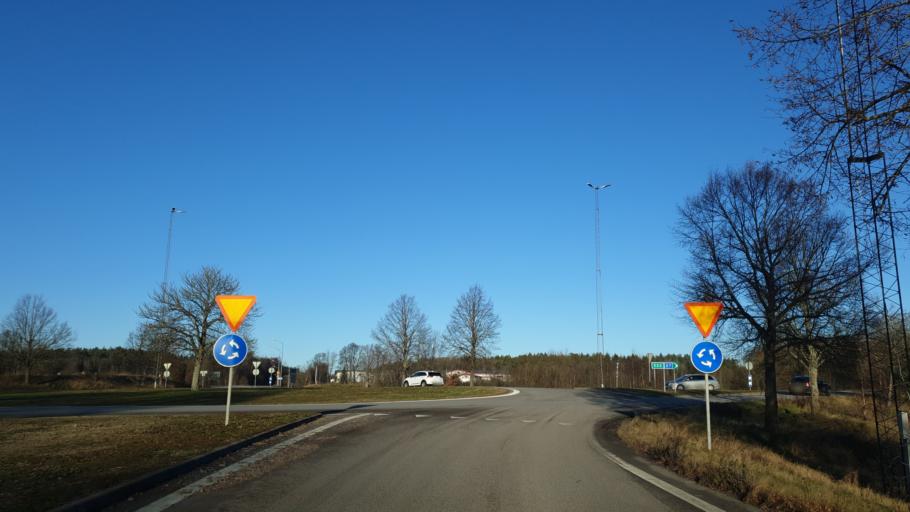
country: SE
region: Blekinge
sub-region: Ronneby Kommun
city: Ronneby
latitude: 56.2017
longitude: 15.3105
